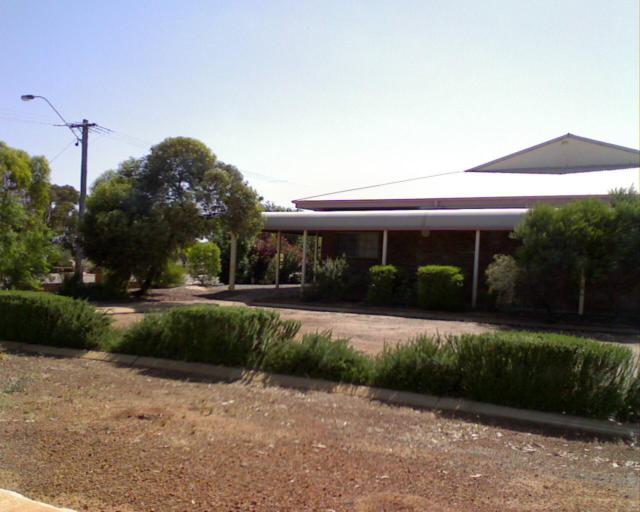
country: AU
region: Western Australia
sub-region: Merredin
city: Merredin
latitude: -30.9149
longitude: 118.2028
